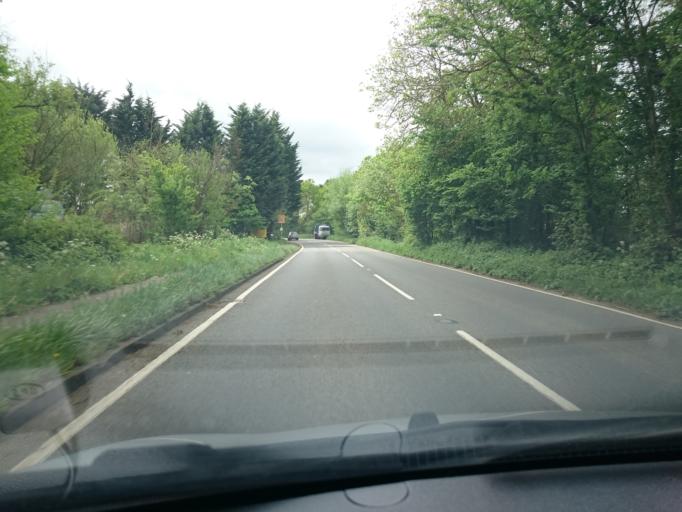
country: GB
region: England
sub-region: Surrey
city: Normandy
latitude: 51.2598
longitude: -0.6537
